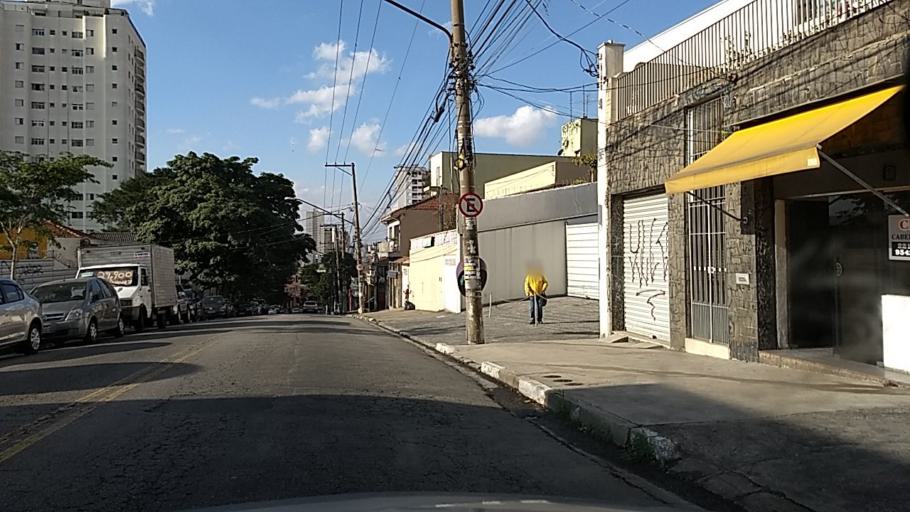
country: BR
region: Sao Paulo
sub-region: Sao Paulo
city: Sao Paulo
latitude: -23.4919
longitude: -46.5970
